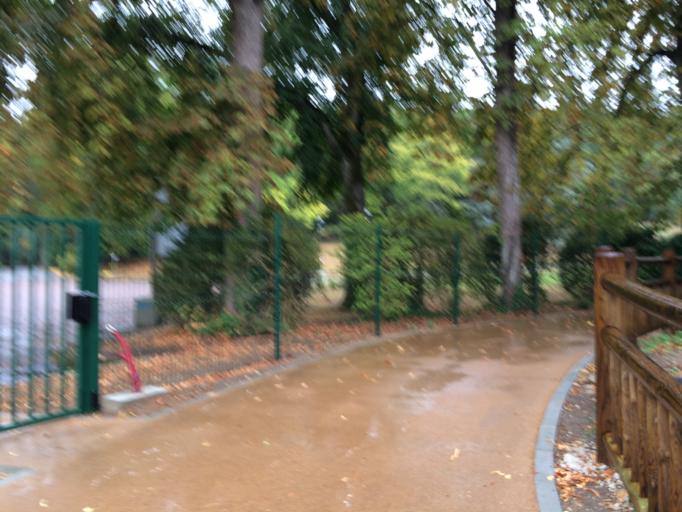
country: FR
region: Ile-de-France
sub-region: Departement de l'Essonne
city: Gif-sur-Yvette
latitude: 48.7029
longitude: 2.1352
